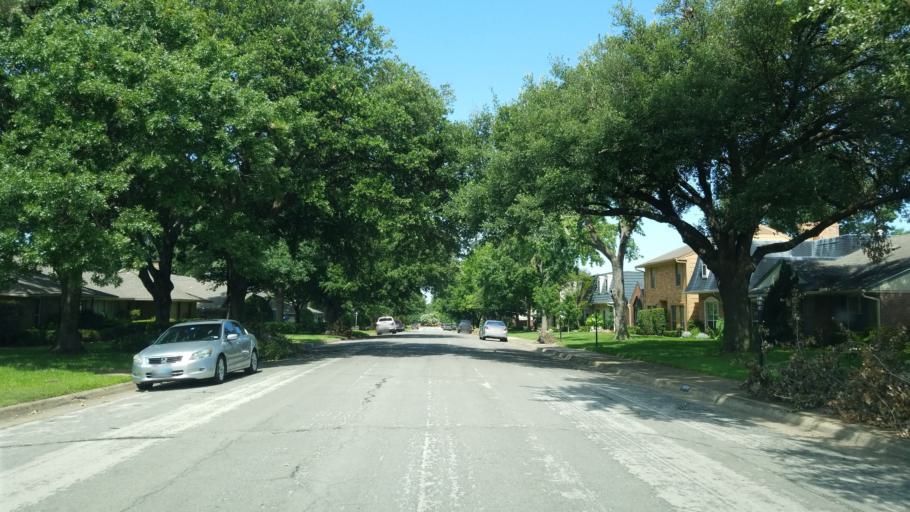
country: US
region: Texas
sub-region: Dallas County
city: Farmers Branch
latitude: 32.9075
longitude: -96.8523
